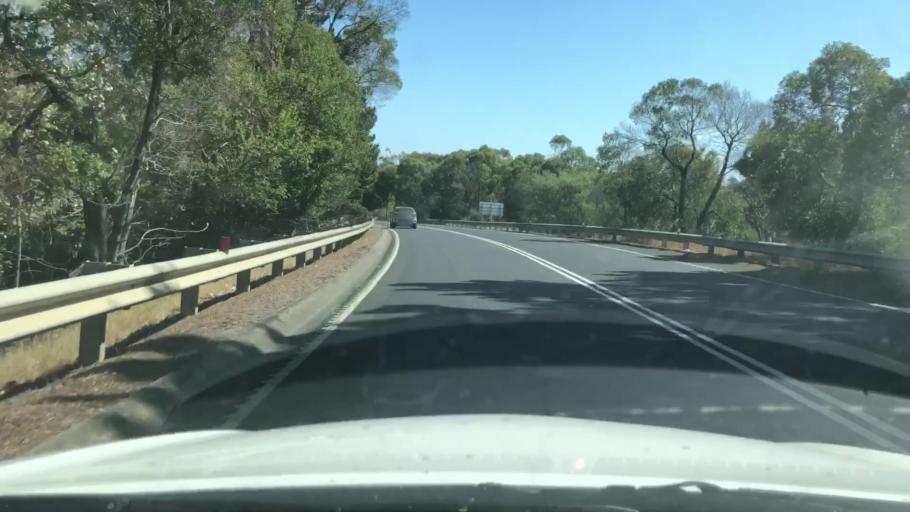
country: AU
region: Victoria
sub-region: Yarra Ranges
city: Selby
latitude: -37.9385
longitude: 145.3836
